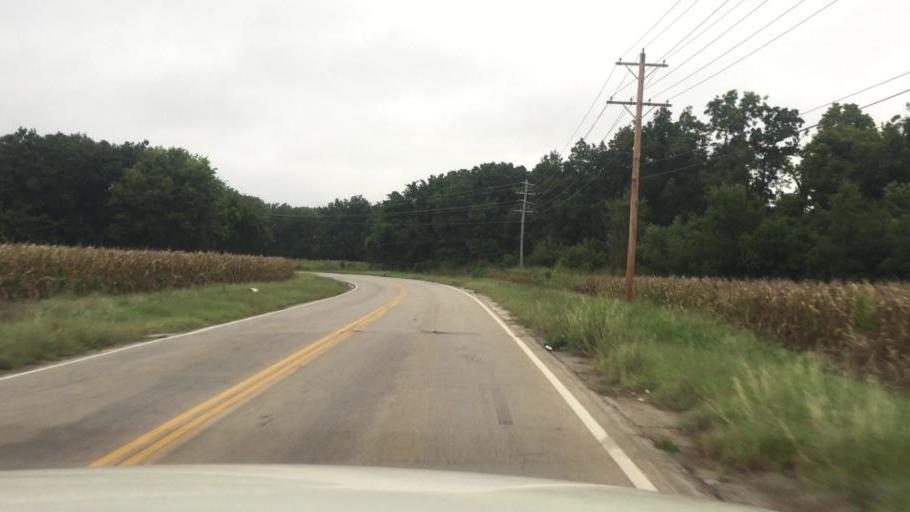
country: US
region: Kansas
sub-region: Montgomery County
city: Coffeyville
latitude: 37.0350
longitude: -95.5829
